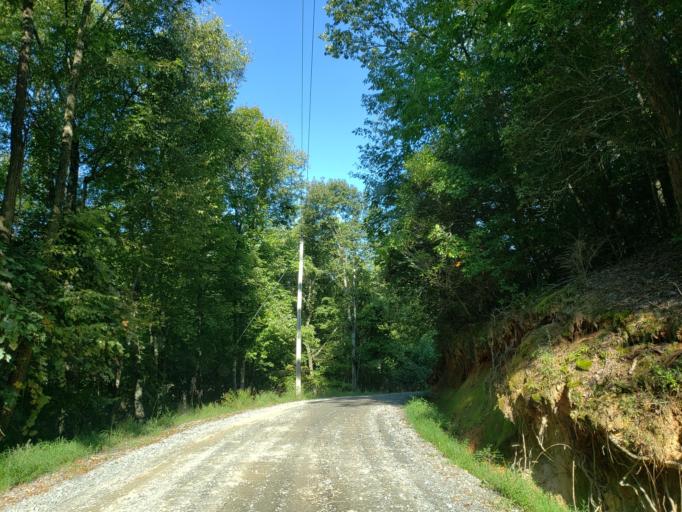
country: US
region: Georgia
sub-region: Fannin County
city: Blue Ridge
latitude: 34.6817
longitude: -84.2617
